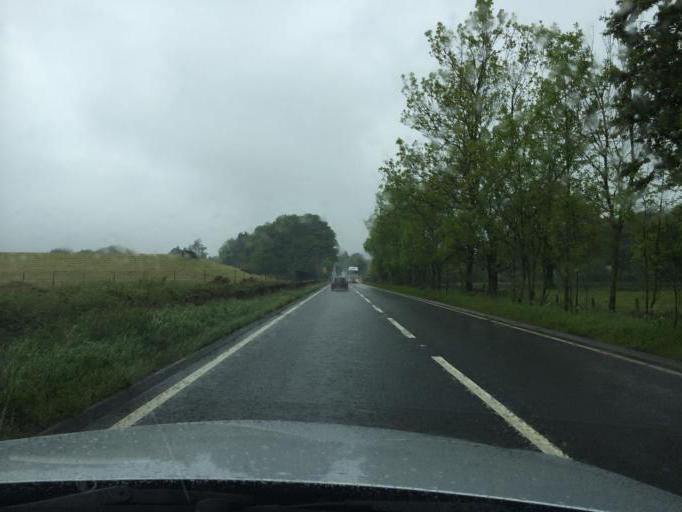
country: GB
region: England
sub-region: Barnsley
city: Penistone
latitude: 53.5008
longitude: -1.6721
